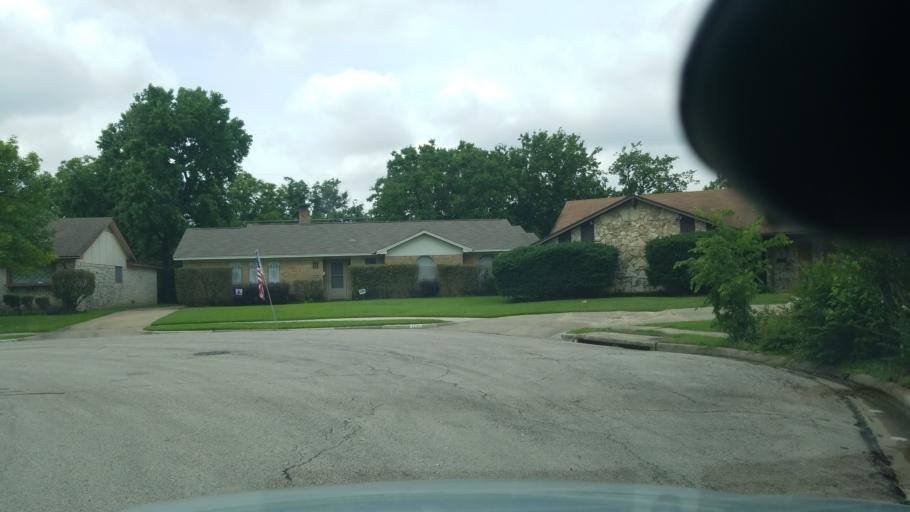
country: US
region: Texas
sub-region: Dallas County
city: Irving
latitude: 32.8475
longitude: -96.9630
